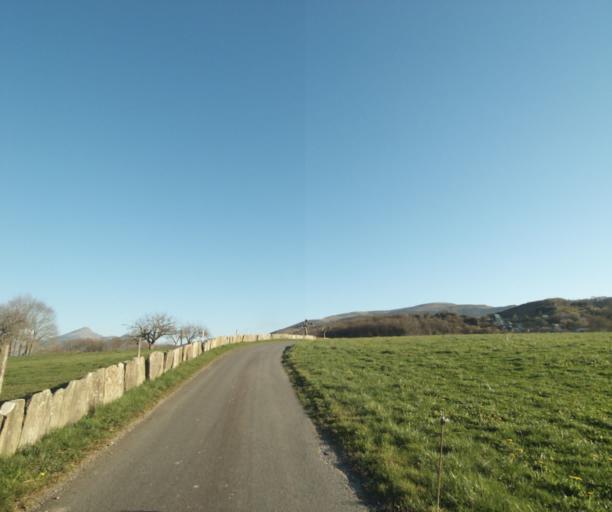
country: FR
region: Aquitaine
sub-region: Departement des Pyrenees-Atlantiques
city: Urrugne
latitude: 43.3535
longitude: -1.7249
